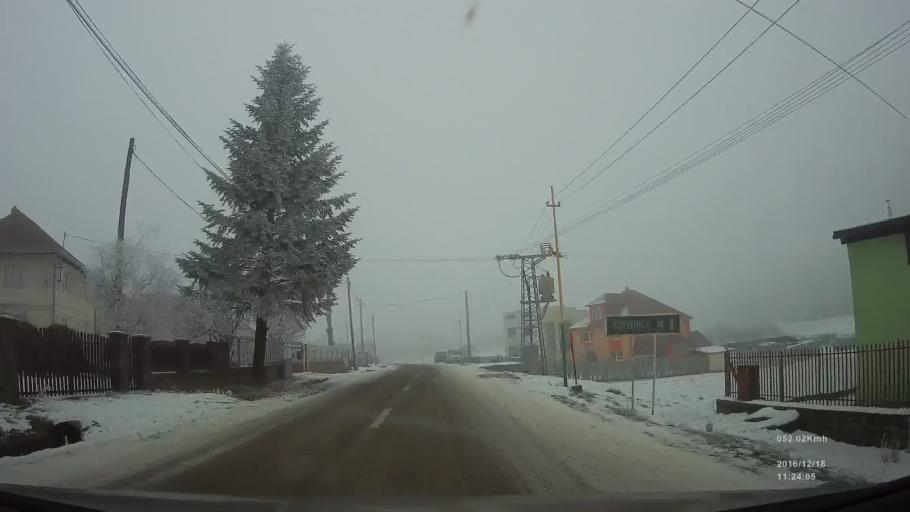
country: SK
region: Presovsky
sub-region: Okres Presov
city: Presov
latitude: 48.8957
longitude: 21.3995
